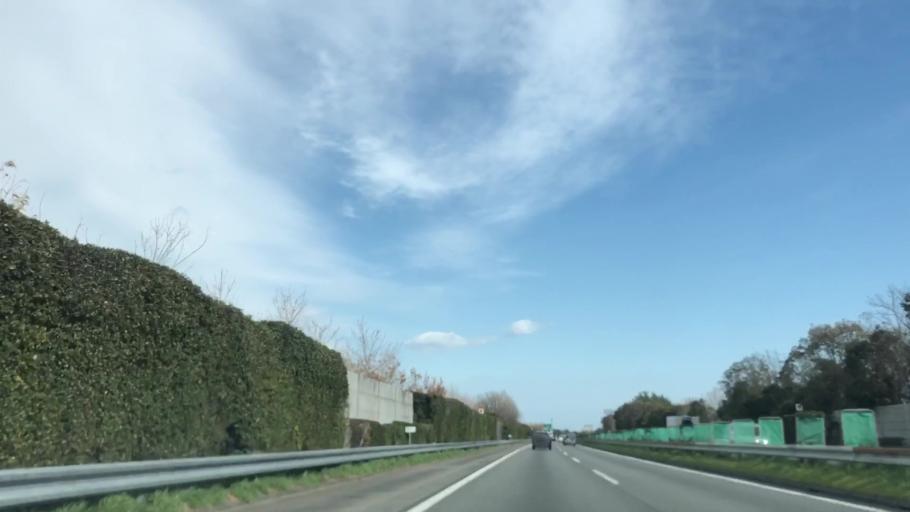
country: JP
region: Shizuoka
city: Hamakita
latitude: 34.7486
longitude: 137.7750
